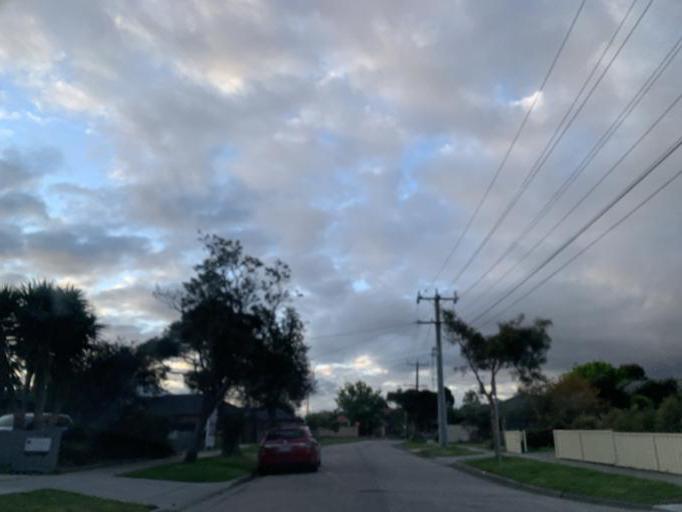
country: AU
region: Victoria
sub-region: Kingston
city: Aspendale
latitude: -38.0195
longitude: 145.1022
